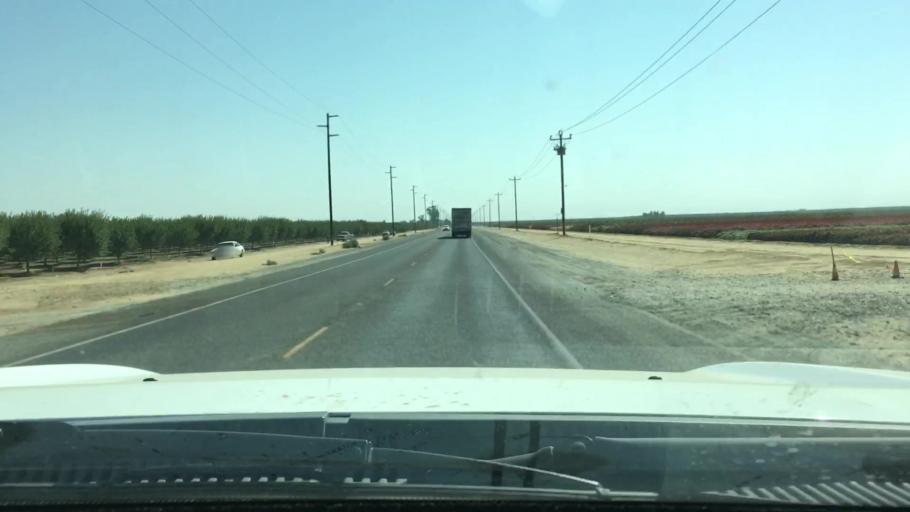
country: US
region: California
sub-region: Kern County
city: Lost Hills
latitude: 35.6011
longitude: -119.5462
